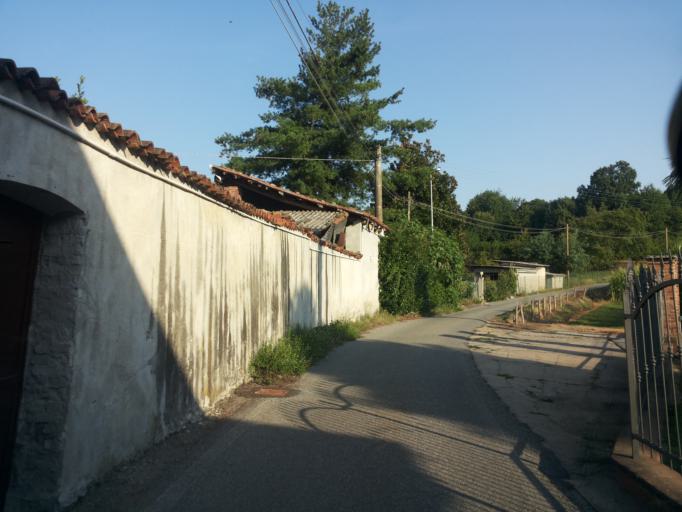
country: IT
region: Piedmont
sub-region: Provincia di Biella
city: Roppolo
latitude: 45.4041
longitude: 8.0614
